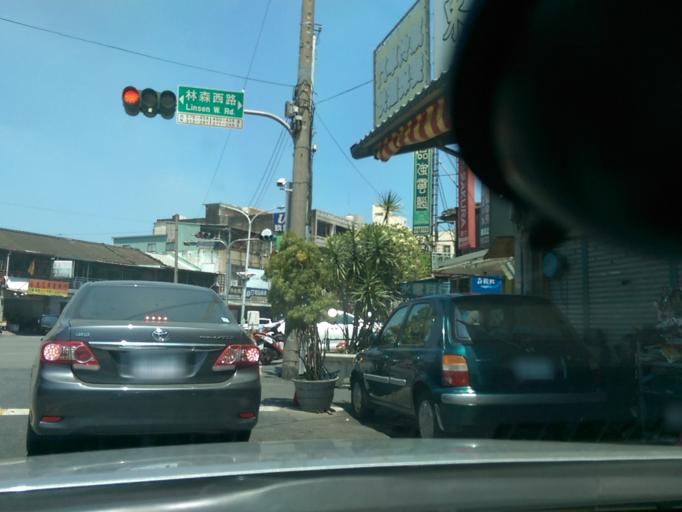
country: TW
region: Taiwan
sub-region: Chiayi
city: Jiayi Shi
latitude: 23.4809
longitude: 120.4440
